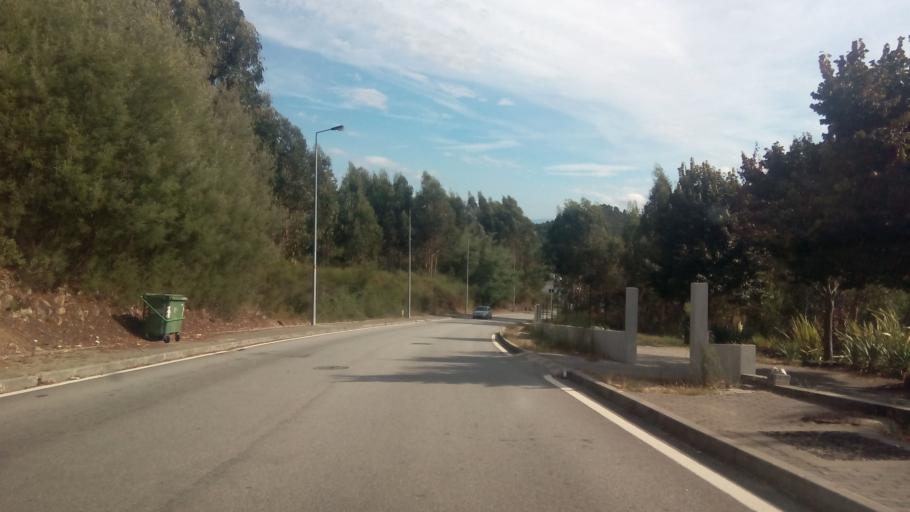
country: PT
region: Porto
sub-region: Paredes
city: Rebordosa
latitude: 41.1959
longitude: -8.4038
